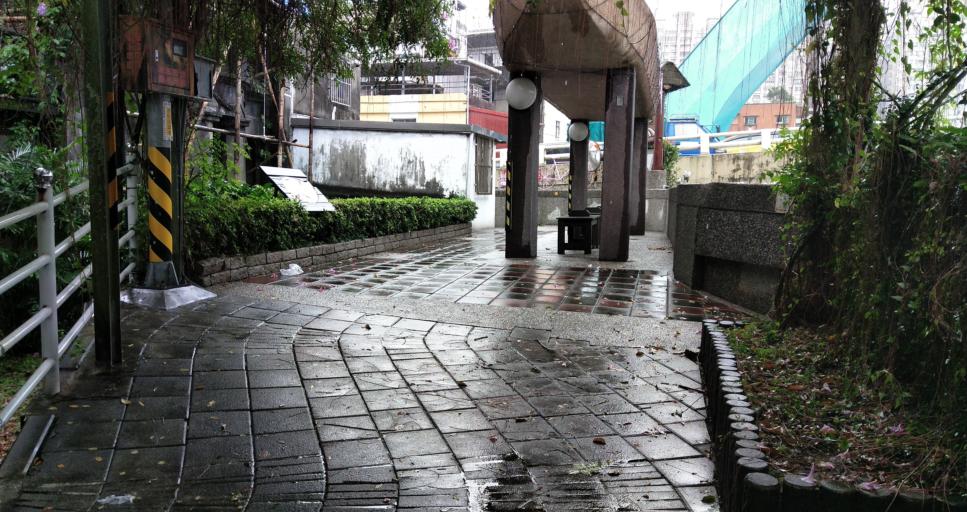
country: TW
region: Taiwan
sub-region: Keelung
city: Keelung
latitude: 25.0685
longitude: 121.6563
